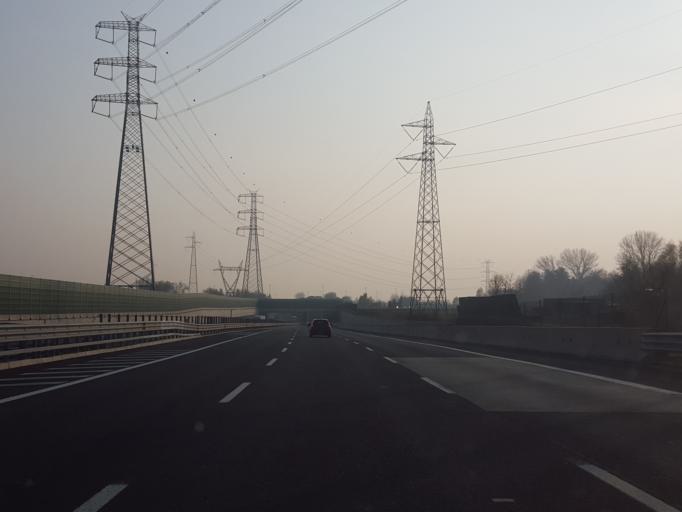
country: IT
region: Veneto
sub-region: Provincia di Venezia
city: Spinea-Orgnano
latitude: 45.5002
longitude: 12.1387
